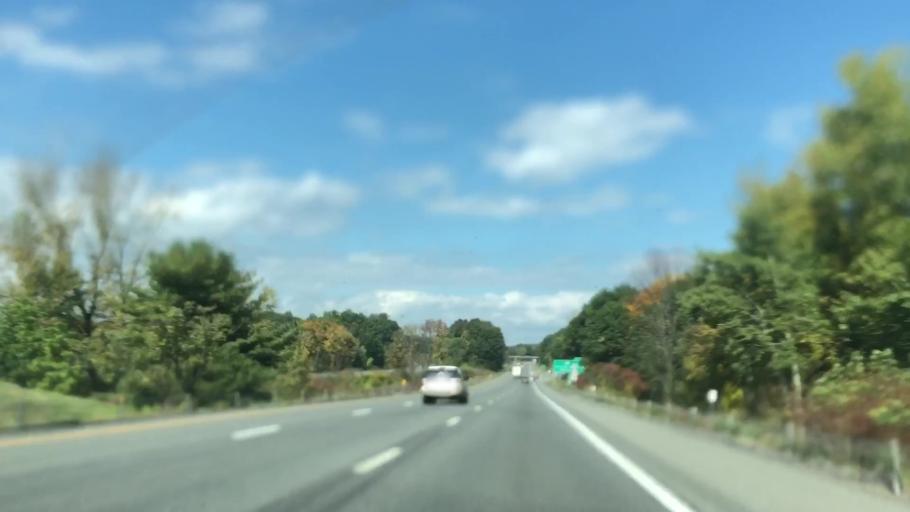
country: US
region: New York
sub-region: Saratoga County
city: Saratoga Springs
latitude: 43.0896
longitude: -73.7499
